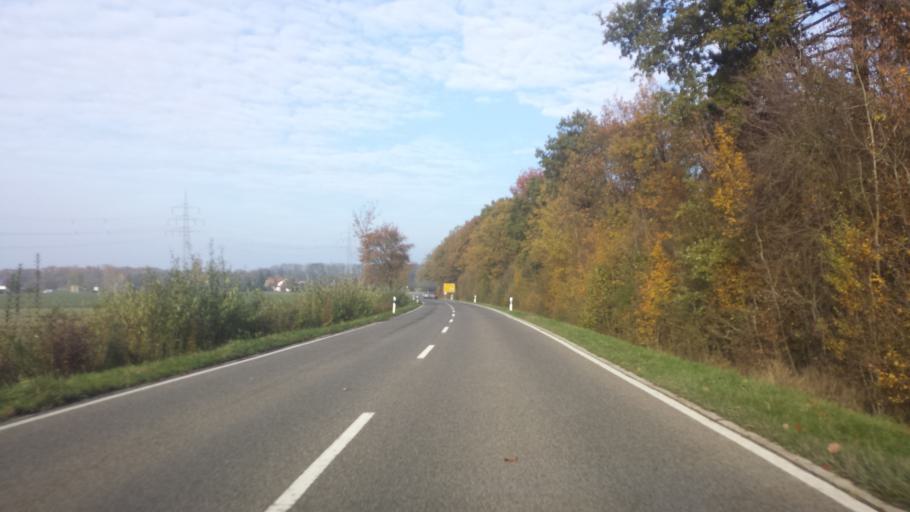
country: DE
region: Baden-Wuerttemberg
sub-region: Karlsruhe Region
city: Huffenhardt
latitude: 49.3171
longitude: 9.0743
